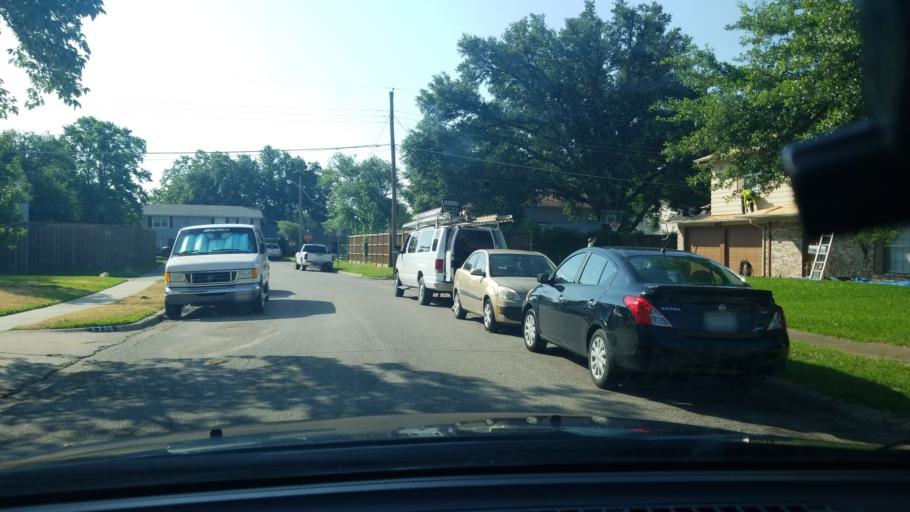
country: US
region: Texas
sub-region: Dallas County
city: Mesquite
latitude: 32.8223
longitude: -96.6400
